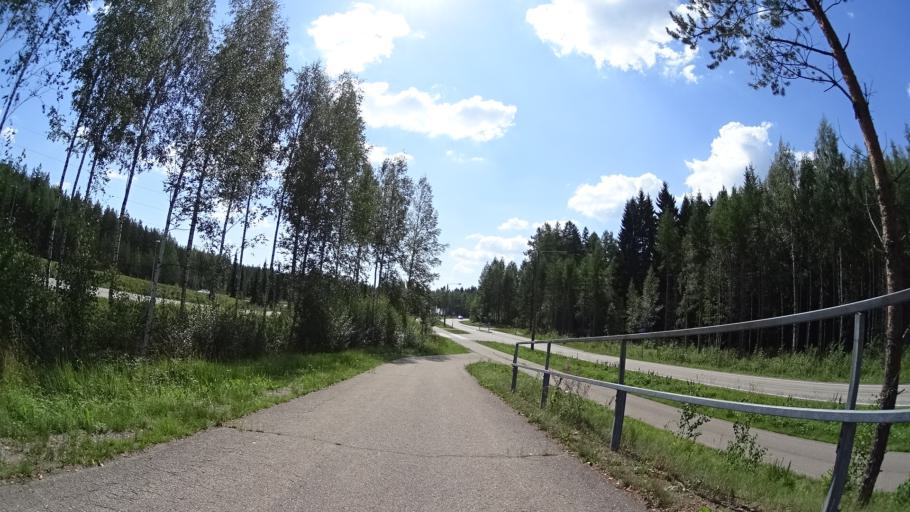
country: FI
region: Uusimaa
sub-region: Helsinki
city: Tuusula
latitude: 60.3577
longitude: 24.9996
